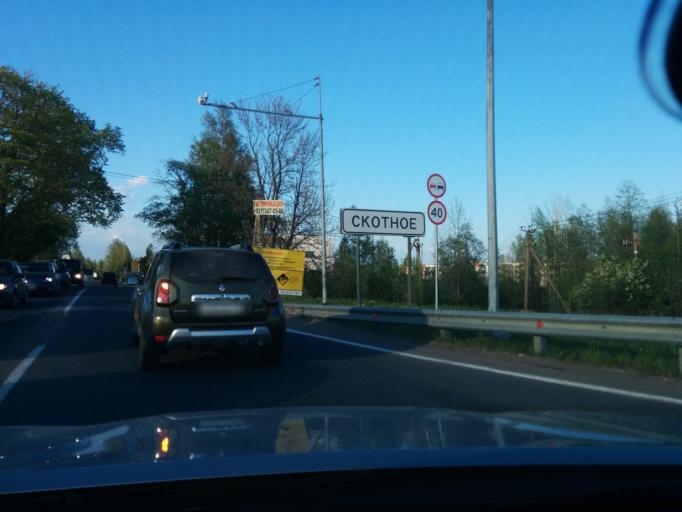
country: RU
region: Leningrad
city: Luppolovo
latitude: 60.1770
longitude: 30.3606
